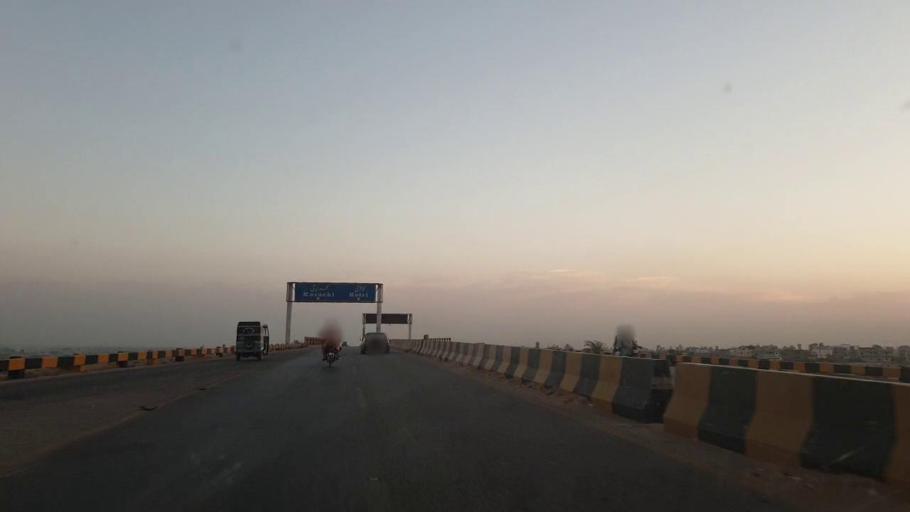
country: PK
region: Sindh
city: Jamshoro
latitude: 25.4008
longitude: 68.2725
